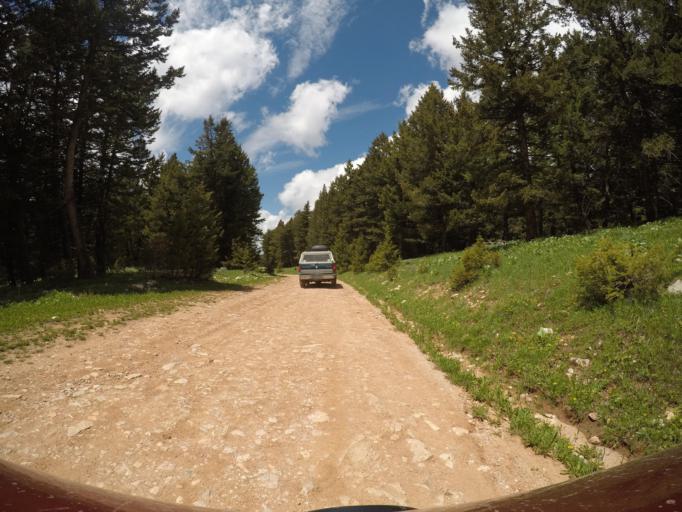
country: US
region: Wyoming
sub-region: Big Horn County
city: Lovell
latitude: 45.1629
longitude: -108.4039
